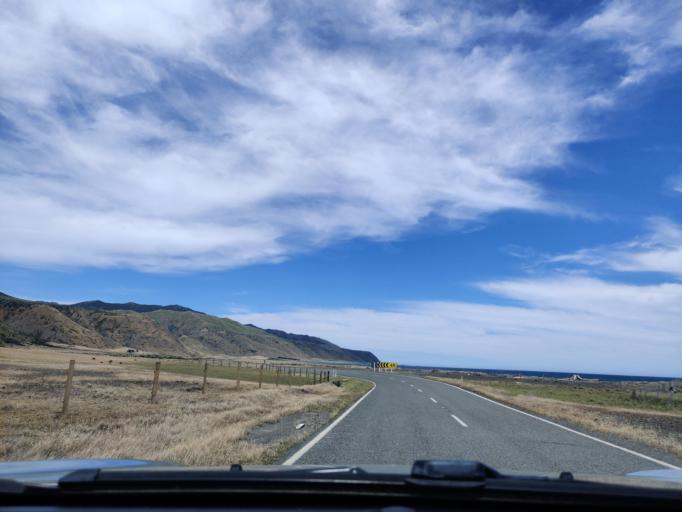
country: NZ
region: Wellington
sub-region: South Wairarapa District
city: Waipawa
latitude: -41.5274
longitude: 175.2008
